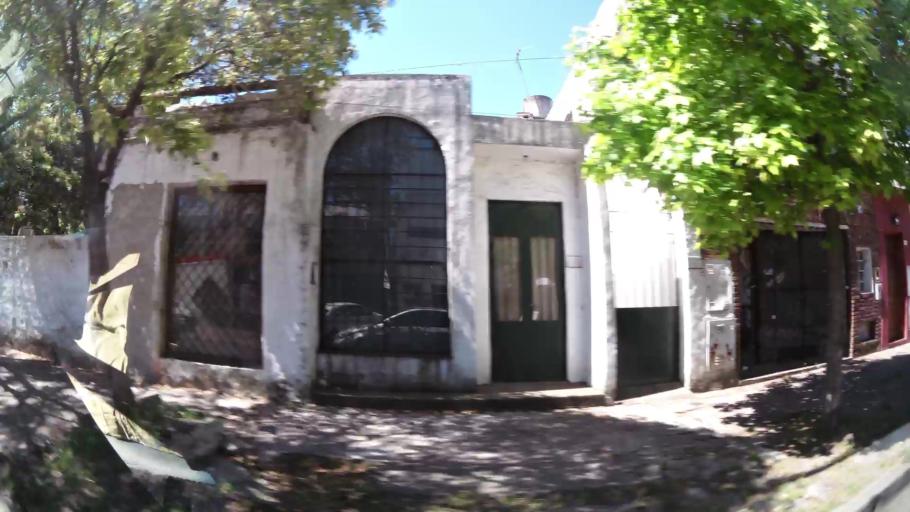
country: AR
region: Buenos Aires
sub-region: Partido de San Isidro
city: San Isidro
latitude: -34.4657
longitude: -58.5071
